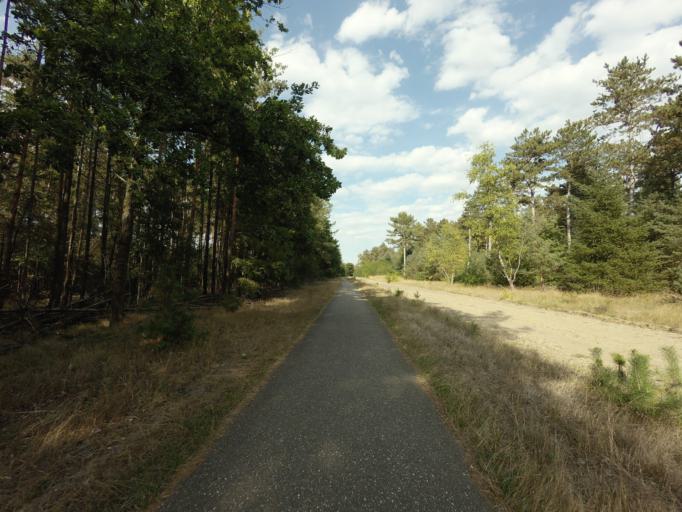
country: NL
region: North Brabant
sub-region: Gemeente Valkenswaard
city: Valkenswaard
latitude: 51.3219
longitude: 5.5178
